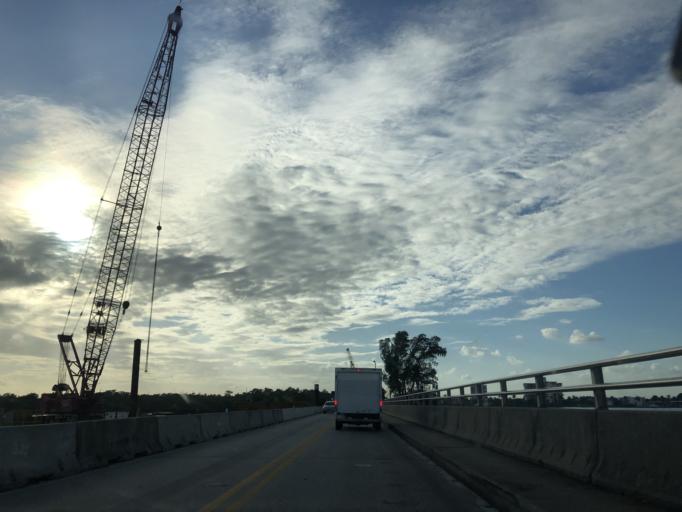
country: US
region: Florida
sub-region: Palm Beach County
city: Palm Beach
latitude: 26.6760
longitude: -80.0403
